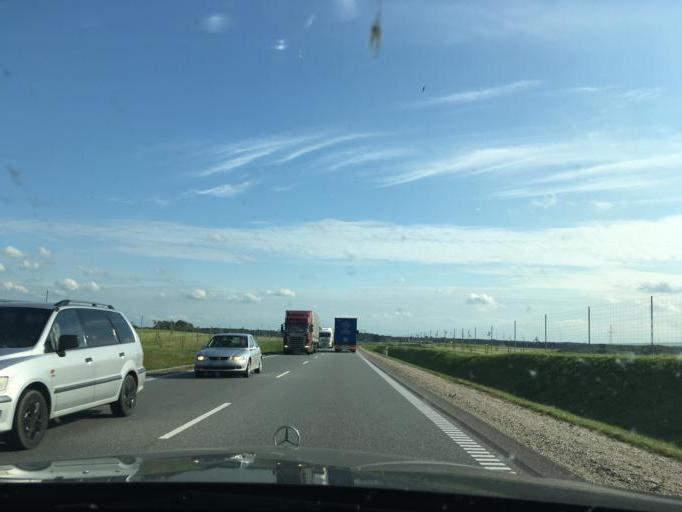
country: PL
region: Podlasie
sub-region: Powiat suwalski
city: Raczki
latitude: 53.8927
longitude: 22.8638
